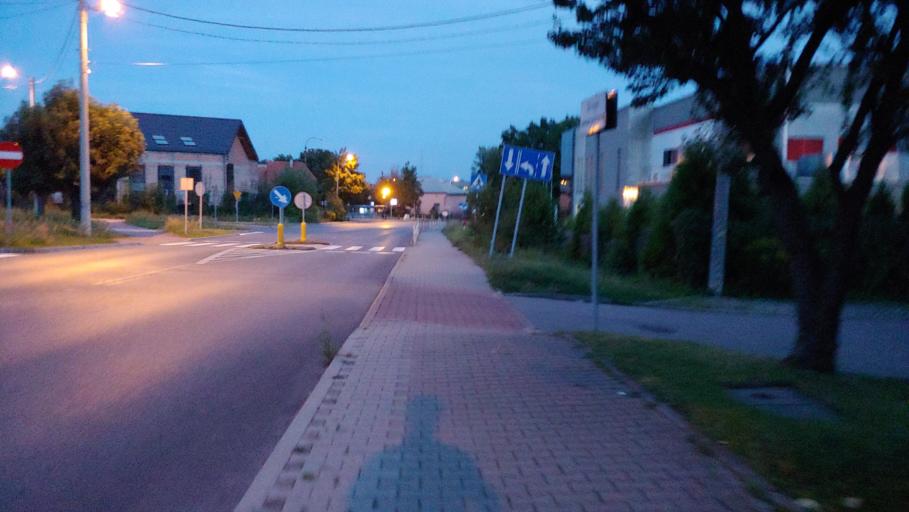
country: PL
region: Lesser Poland Voivodeship
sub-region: Powiat chrzanowski
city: Trzebinia
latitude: 50.1604
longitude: 19.4651
